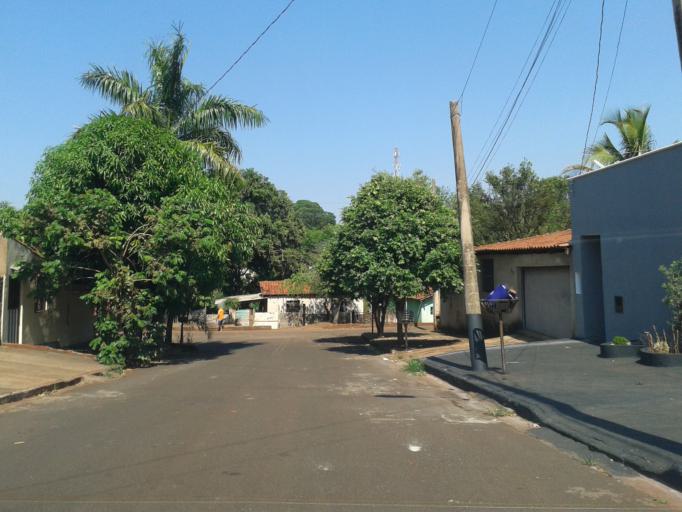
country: BR
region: Minas Gerais
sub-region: Ituiutaba
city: Ituiutaba
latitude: -18.9567
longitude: -49.4531
